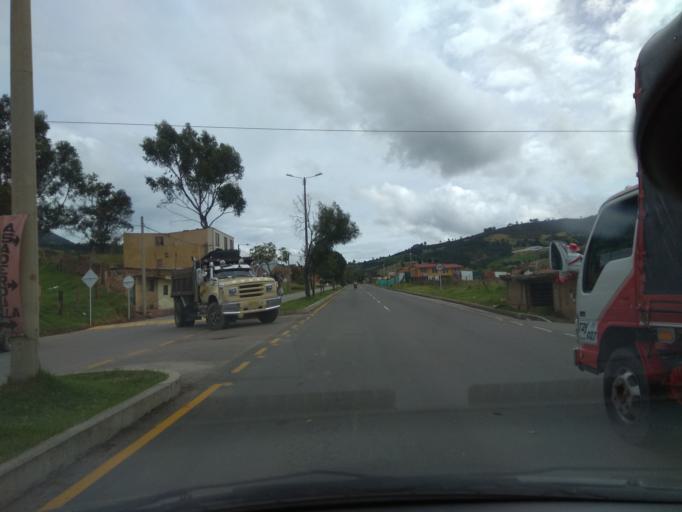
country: CO
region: Boyaca
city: Santa Rosa de Viterbo
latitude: 5.8767
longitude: -72.9853
